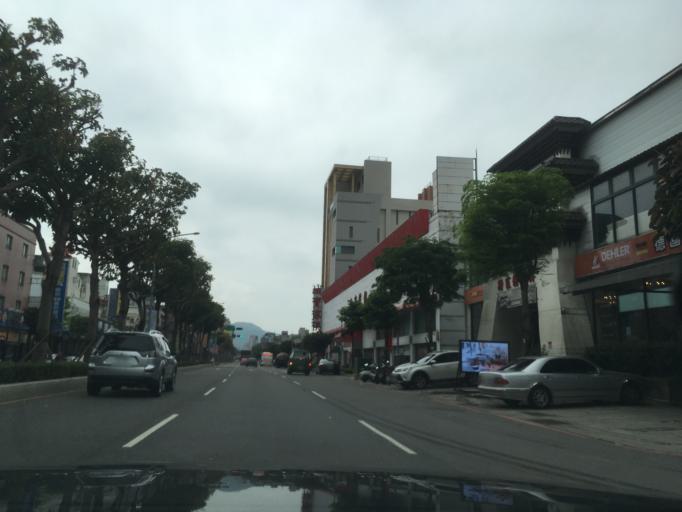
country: TW
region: Taipei
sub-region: Taipei
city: Banqiao
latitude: 24.9834
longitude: 121.4417
